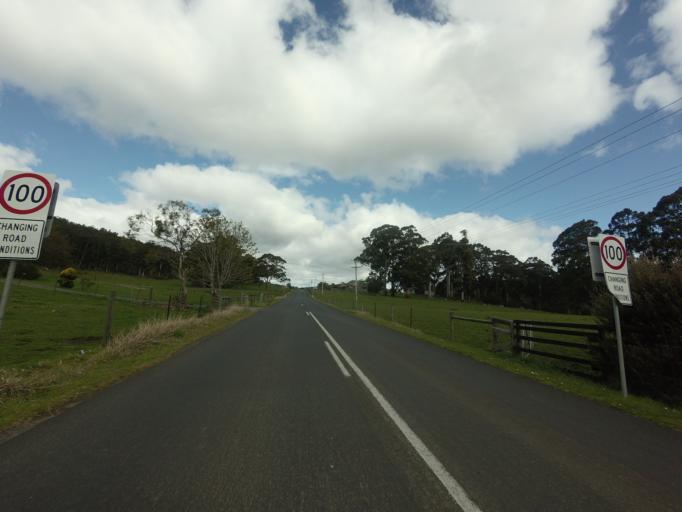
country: AU
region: Tasmania
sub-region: Huon Valley
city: Geeveston
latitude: -43.1793
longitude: 146.9258
